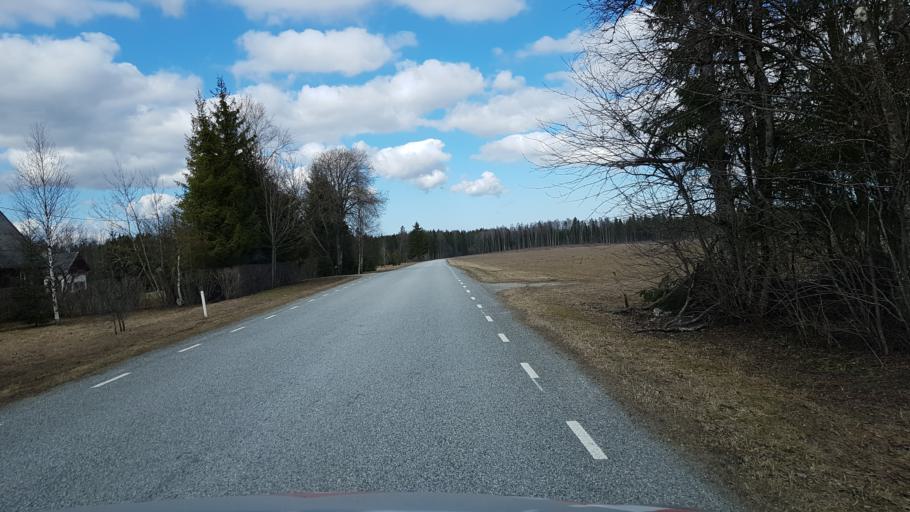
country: EE
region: Laeaene-Virumaa
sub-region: Tamsalu vald
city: Tamsalu
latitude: 59.2236
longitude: 26.1632
